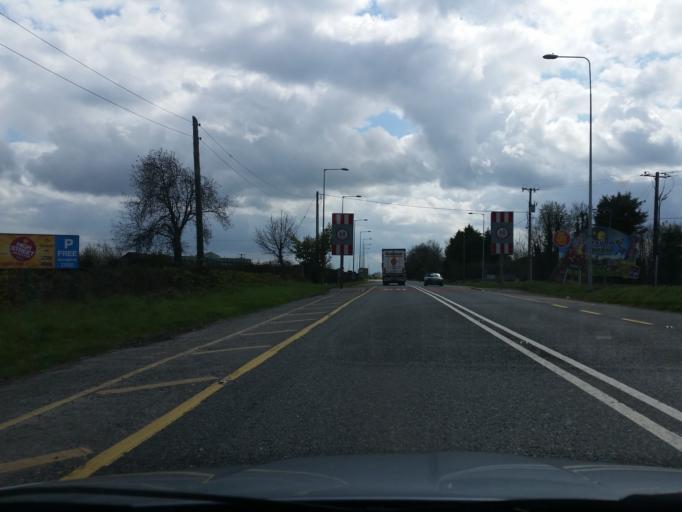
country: IE
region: Leinster
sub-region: An Mhi
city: Ashbourne
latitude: 53.5305
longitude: -6.4198
